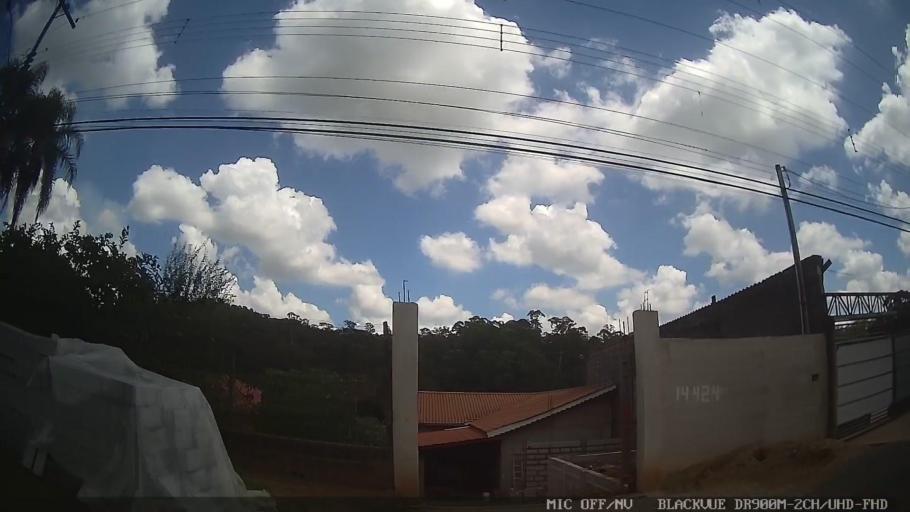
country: BR
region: Sao Paulo
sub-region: Atibaia
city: Atibaia
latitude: -23.1622
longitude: -46.6289
